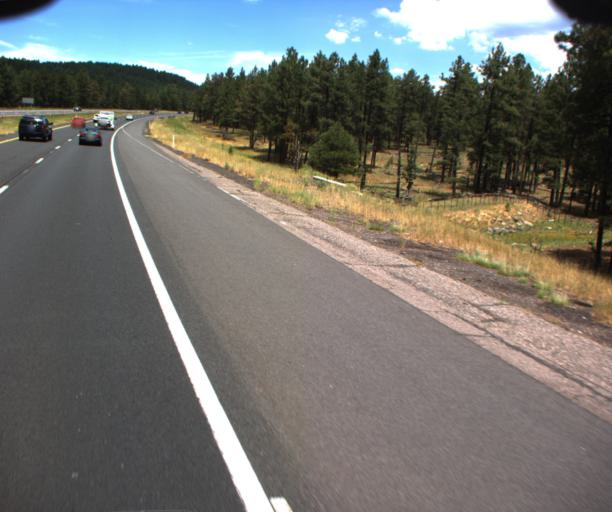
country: US
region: Arizona
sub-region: Coconino County
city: Sedona
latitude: 34.9564
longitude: -111.6762
